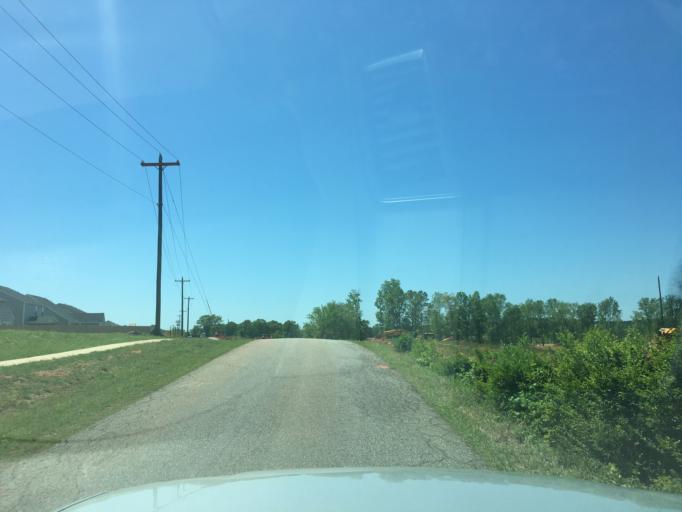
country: US
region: South Carolina
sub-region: Spartanburg County
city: Duncan
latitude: 34.8621
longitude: -82.1517
